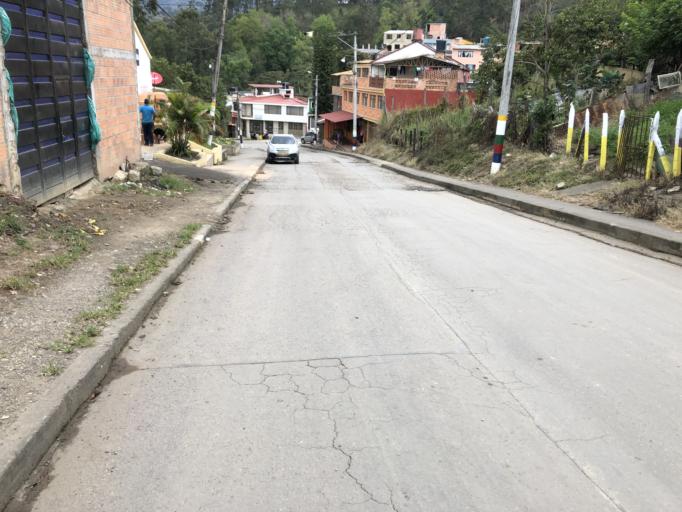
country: CO
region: Cundinamarca
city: Gacheta
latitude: 4.8175
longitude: -73.6394
